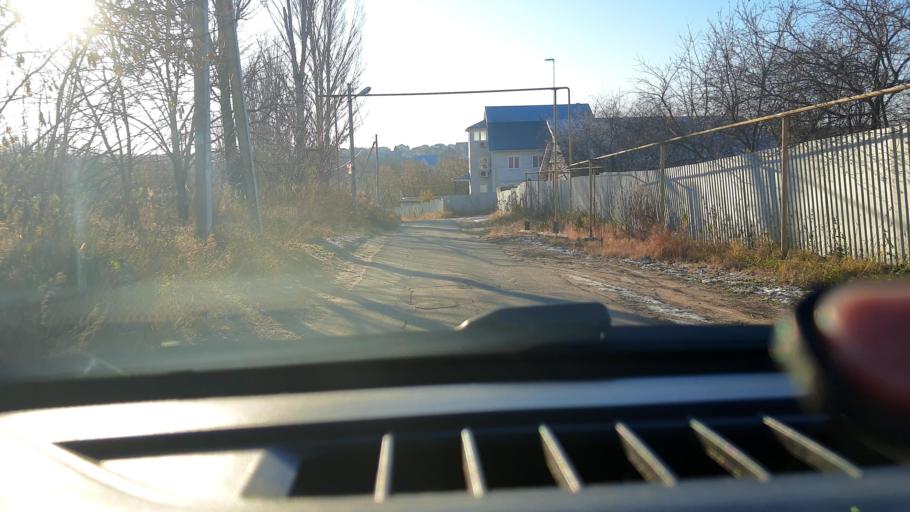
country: RU
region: Nizjnij Novgorod
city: Burevestnik
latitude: 56.2020
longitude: 43.8620
